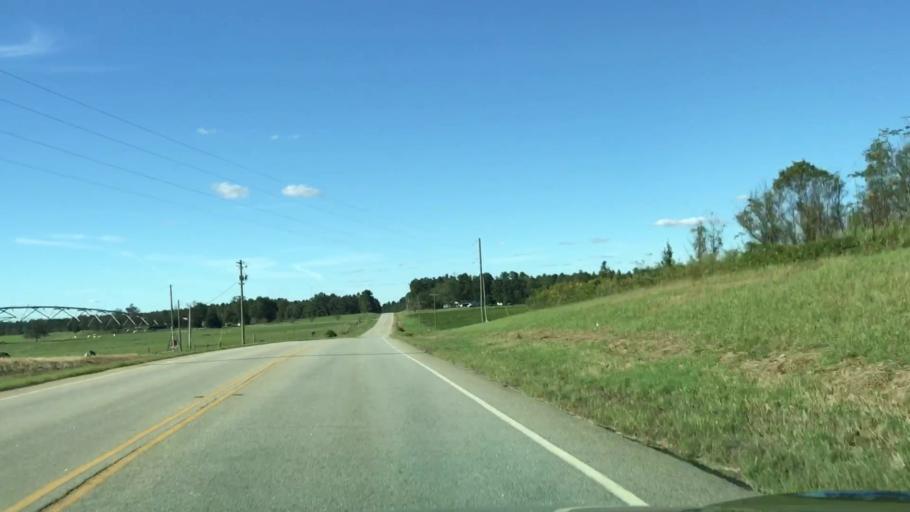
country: US
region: Georgia
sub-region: Jefferson County
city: Louisville
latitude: 33.0782
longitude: -82.4119
